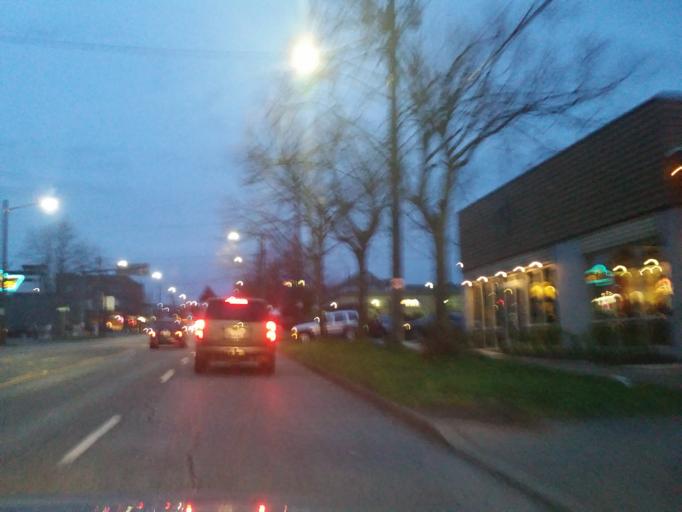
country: US
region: Washington
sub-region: King County
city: Seattle
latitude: 47.6726
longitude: -122.3761
